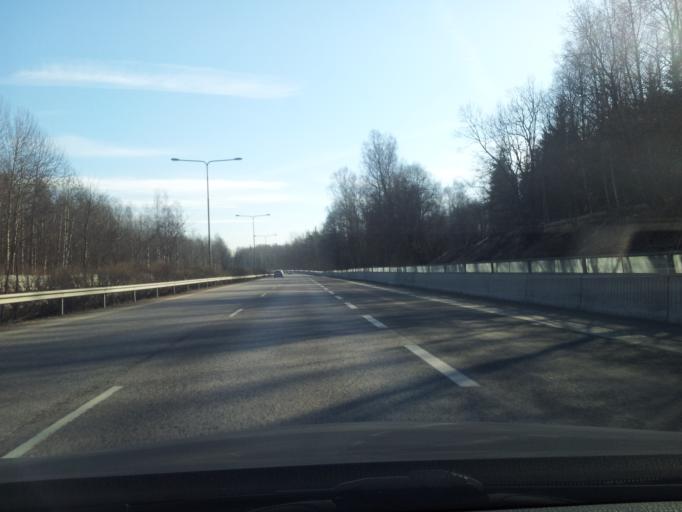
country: FI
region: Uusimaa
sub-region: Helsinki
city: Teekkarikylae
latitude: 60.2035
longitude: 24.8558
